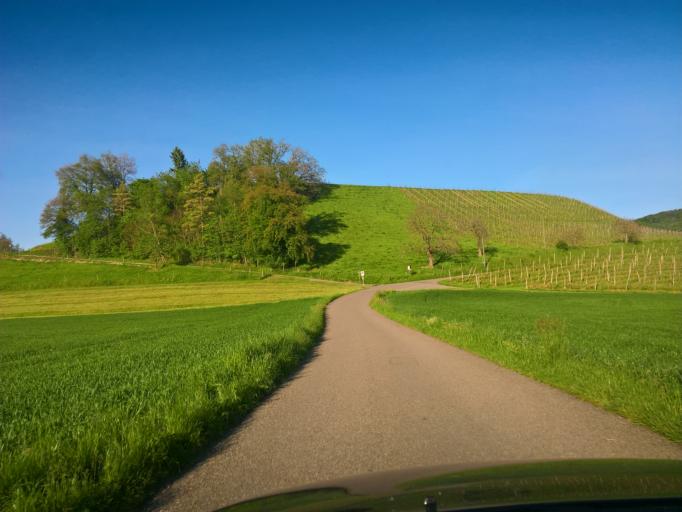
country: CH
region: Zurich
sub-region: Bezirk Buelach
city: Rorbas
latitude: 47.5501
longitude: 8.5582
